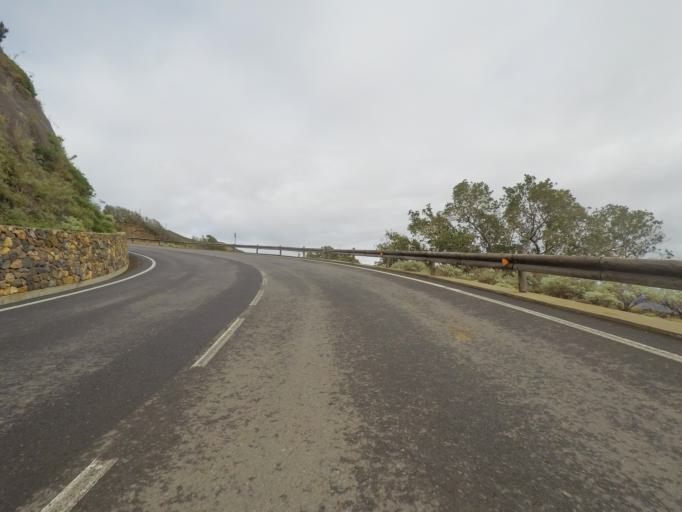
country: ES
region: Canary Islands
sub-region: Provincia de Santa Cruz de Tenerife
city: Vallehermosa
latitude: 28.1631
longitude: -17.2895
